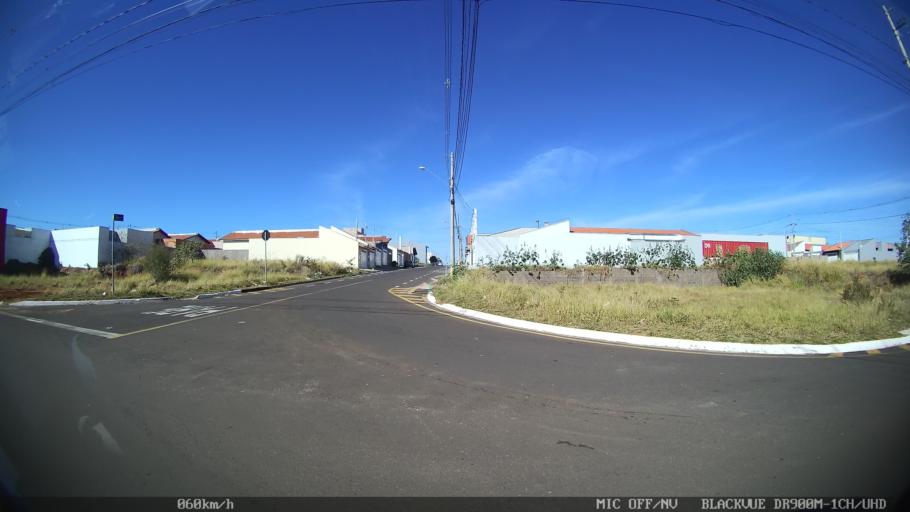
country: BR
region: Sao Paulo
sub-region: Franca
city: Franca
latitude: -20.5644
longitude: -47.3497
